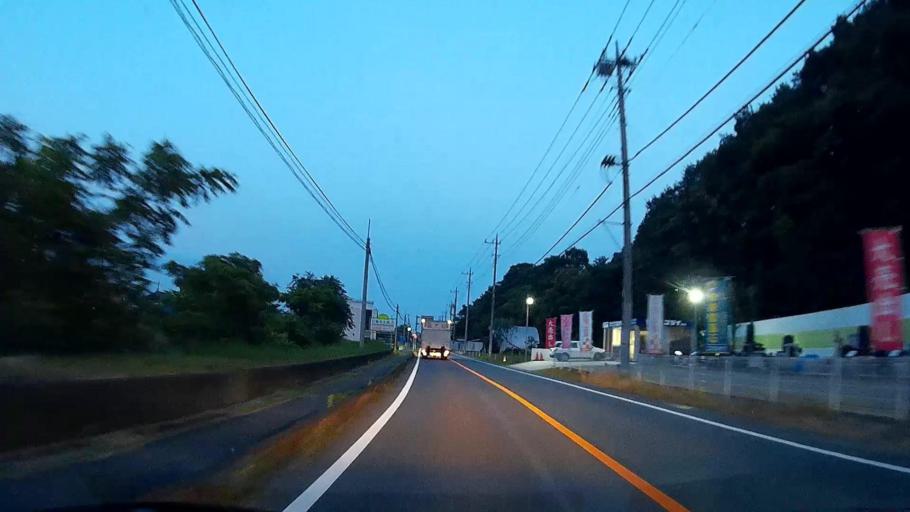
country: JP
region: Gunma
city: Annaka
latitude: 36.3494
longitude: 138.9467
